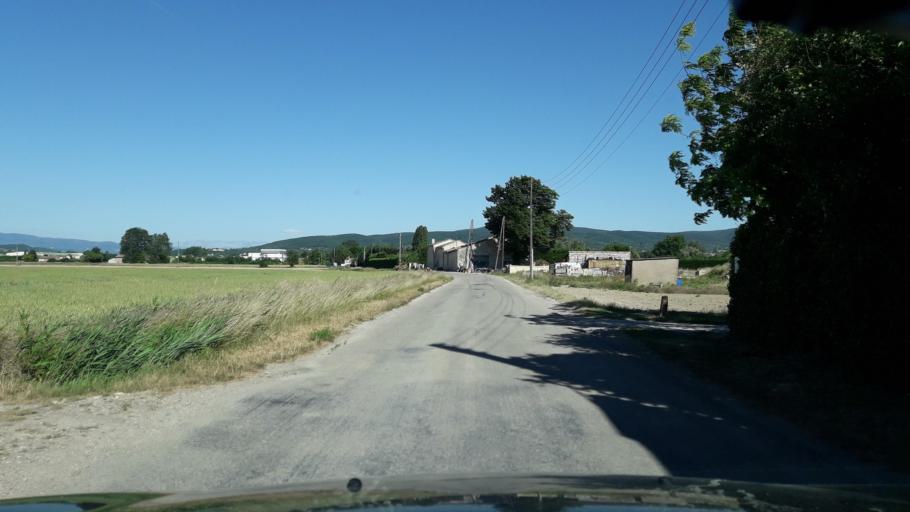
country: FR
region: Rhone-Alpes
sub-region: Departement de l'Ardeche
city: Le Pouzin
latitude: 44.7511
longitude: 4.7793
